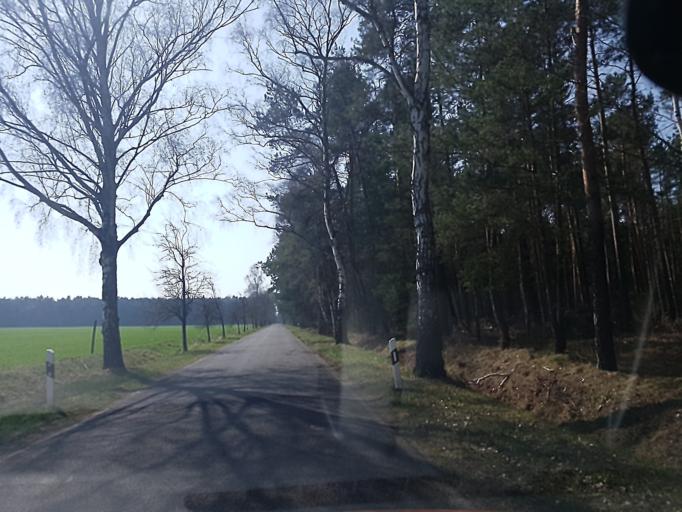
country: DE
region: Saxony
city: Gross Duben
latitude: 51.6596
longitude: 14.5447
